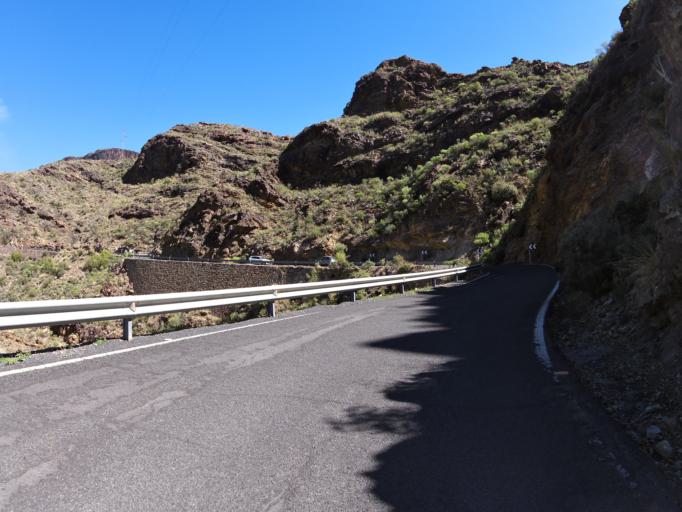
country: ES
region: Canary Islands
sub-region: Provincia de Las Palmas
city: Artenara
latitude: 27.9936
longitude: -15.6937
